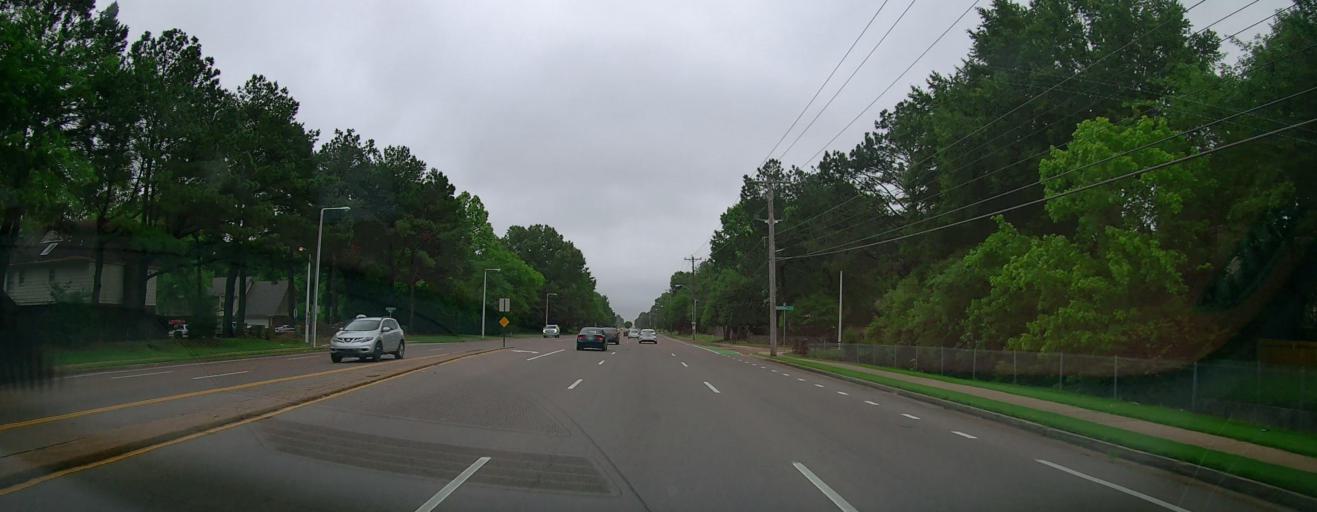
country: US
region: Mississippi
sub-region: De Soto County
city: Olive Branch
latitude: 35.0163
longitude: -89.8313
